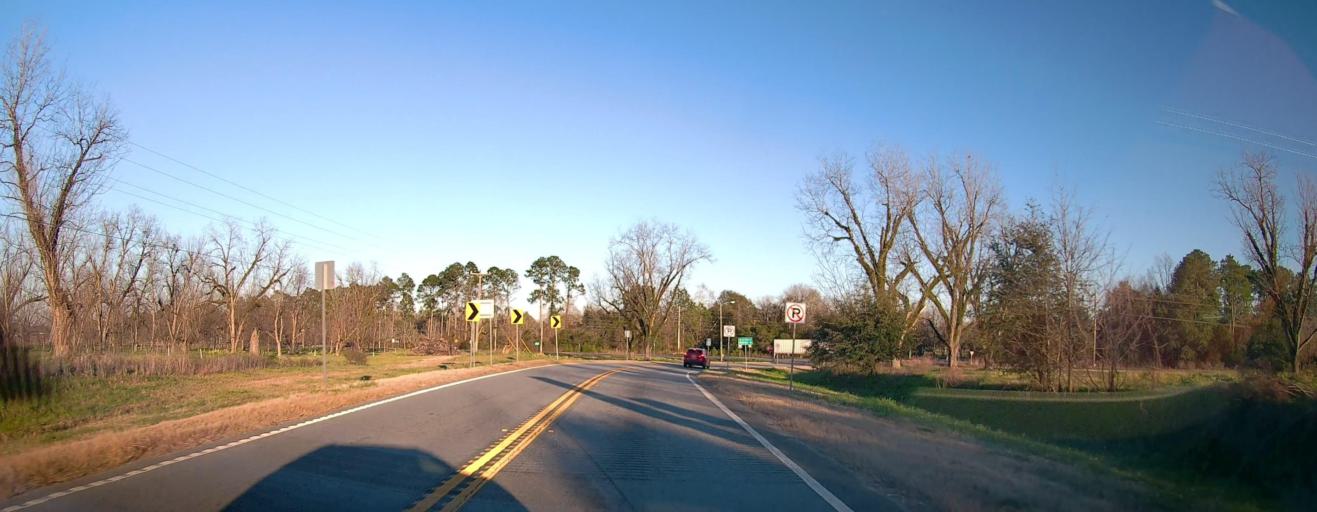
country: US
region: Georgia
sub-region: Dougherty County
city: Albany
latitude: 31.5041
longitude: -84.2122
